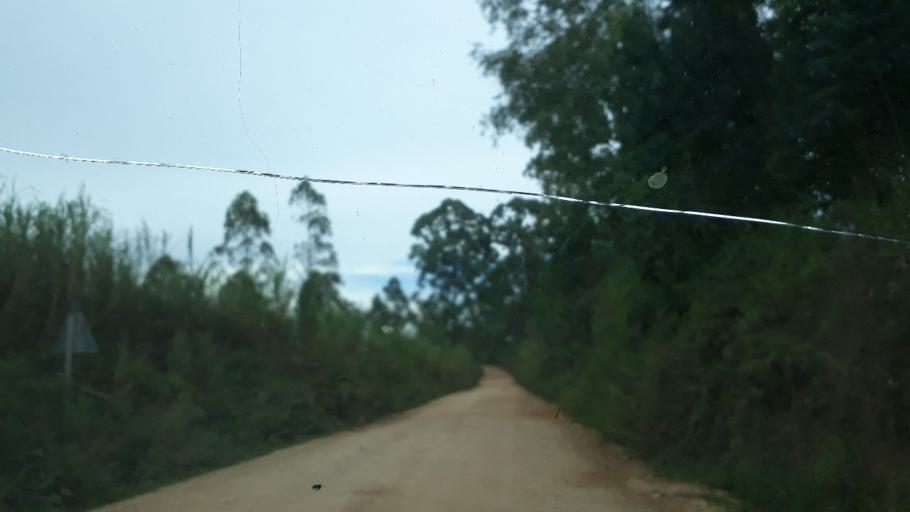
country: CD
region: Eastern Province
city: Bunia
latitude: 1.9212
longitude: 30.5055
